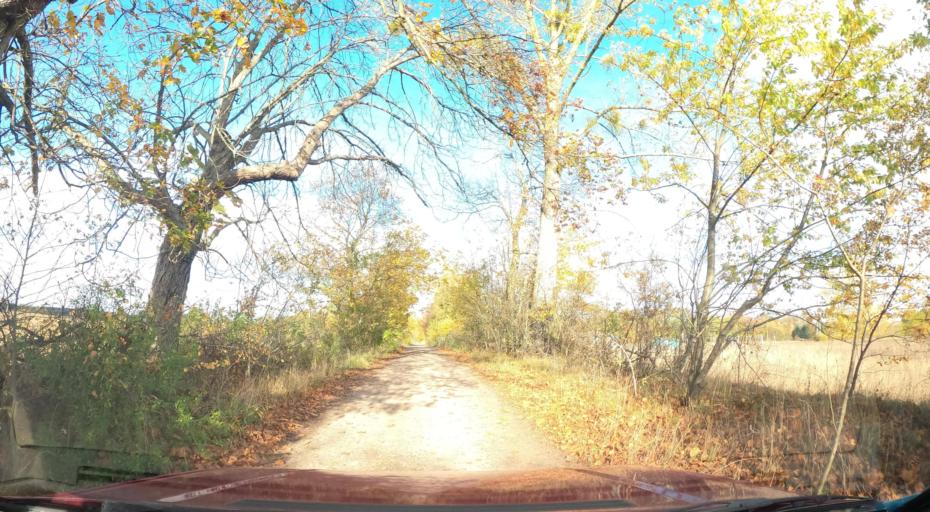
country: PL
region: West Pomeranian Voivodeship
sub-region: Powiat koszalinski
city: Sianow
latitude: 54.1592
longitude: 16.4407
